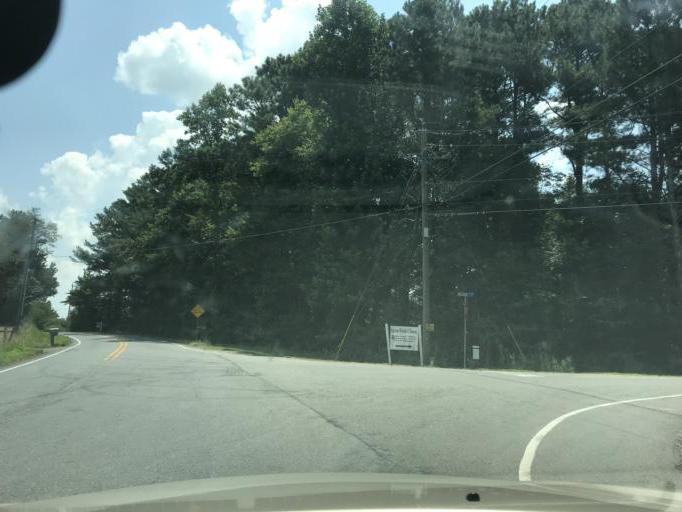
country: US
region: Georgia
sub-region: Dawson County
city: Dawsonville
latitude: 34.3353
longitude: -84.1482
